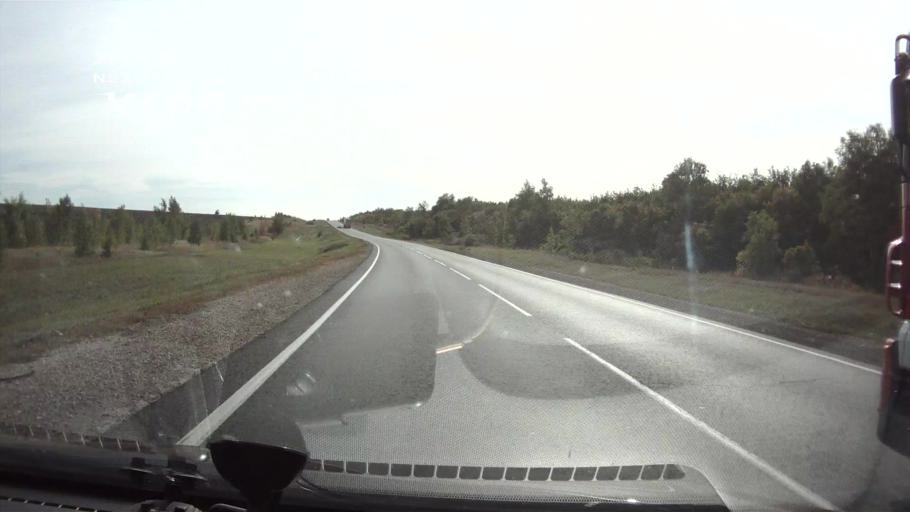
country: RU
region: Saratov
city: Alekseyevka
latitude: 52.2450
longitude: 47.9077
